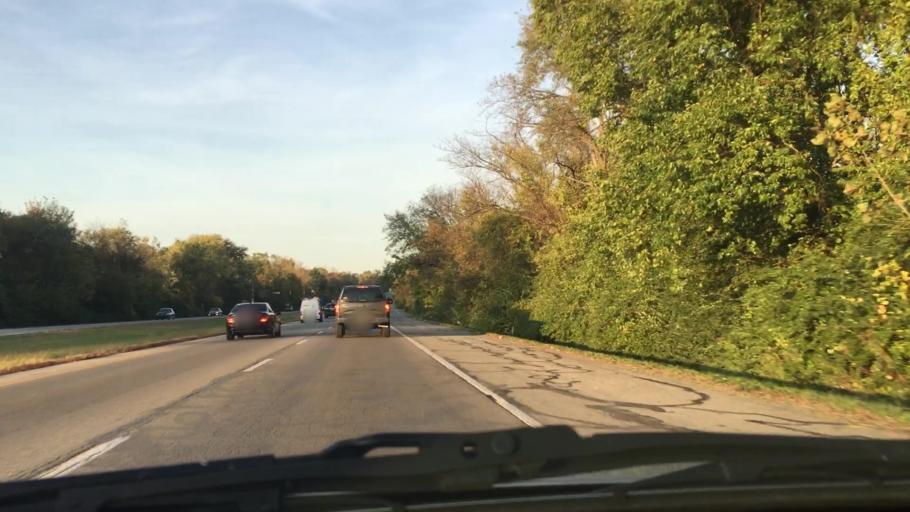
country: US
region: Indiana
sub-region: Marion County
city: Broad Ripple
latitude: 39.8561
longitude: -86.0954
